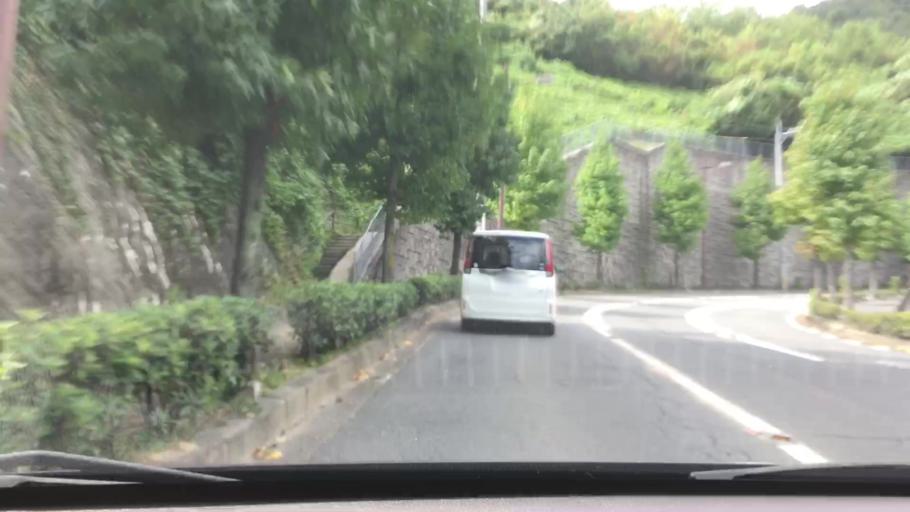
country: JP
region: Hiroshima
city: Hiroshima-shi
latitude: 34.3943
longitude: 132.4123
